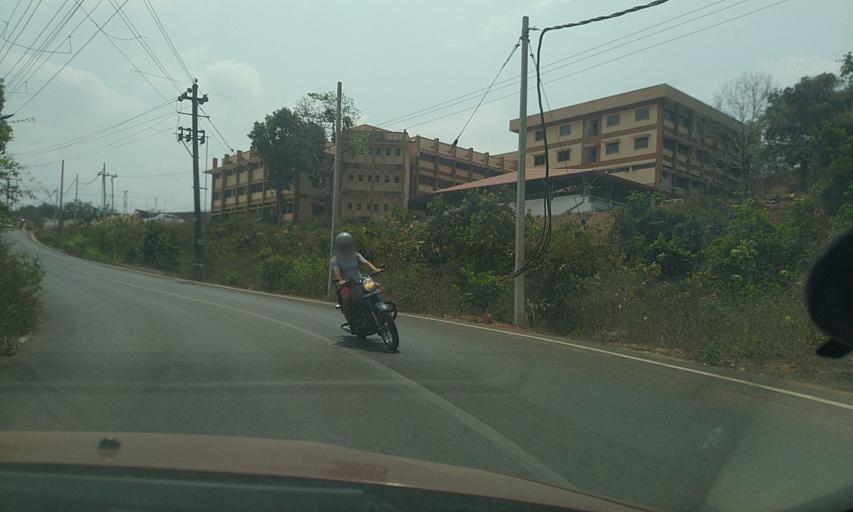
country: IN
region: Goa
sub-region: North Goa
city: Mapuca
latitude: 15.5957
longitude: 73.7944
